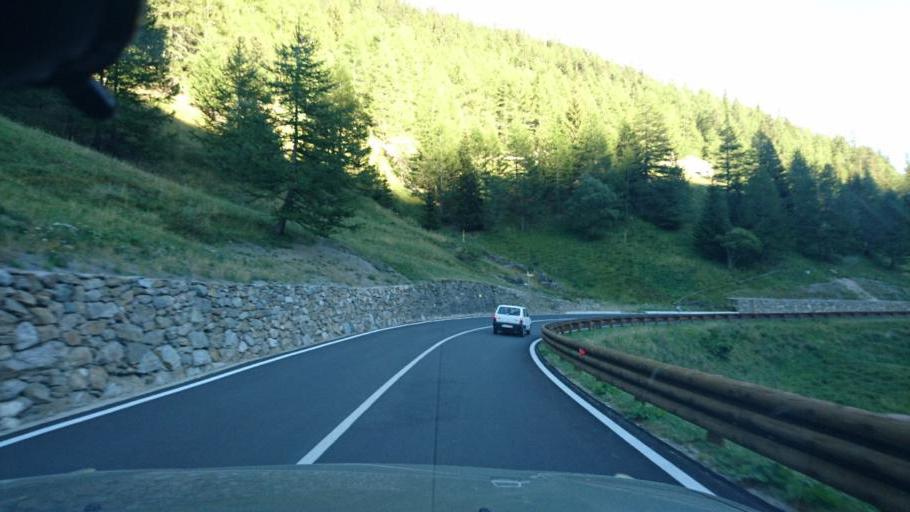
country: IT
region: Aosta Valley
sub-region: Valle d'Aosta
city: San Leonardo
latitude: 45.8430
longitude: 7.1791
